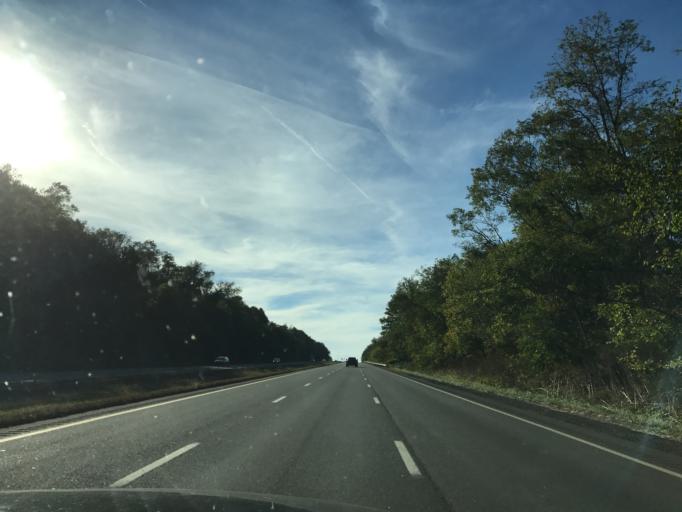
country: US
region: Ohio
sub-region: Belmont County
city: Wolfhurst
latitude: 40.0475
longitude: -80.7750
